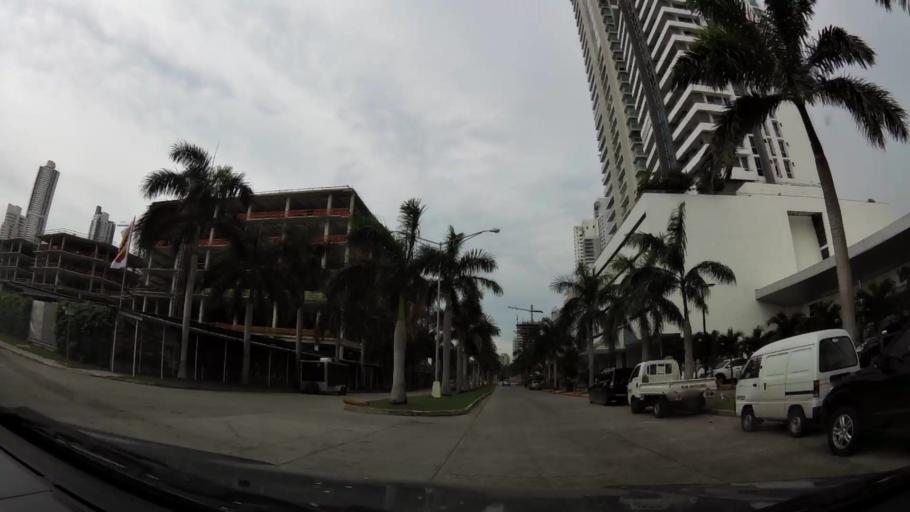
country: PA
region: Panama
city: San Miguelito
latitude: 9.0161
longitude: -79.4641
